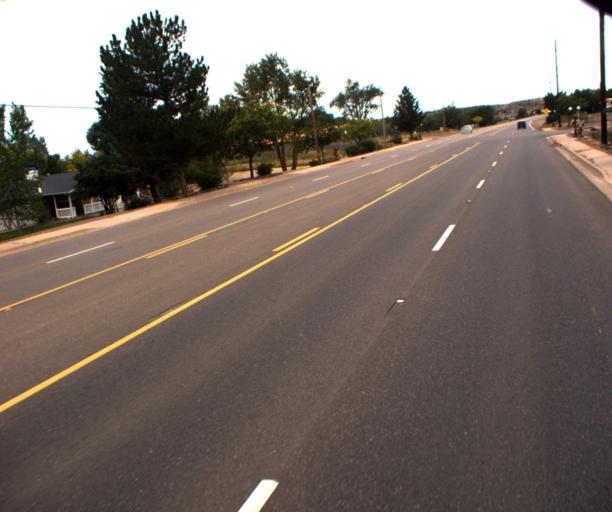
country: US
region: Arizona
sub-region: Navajo County
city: Taylor
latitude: 34.4604
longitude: -110.0912
